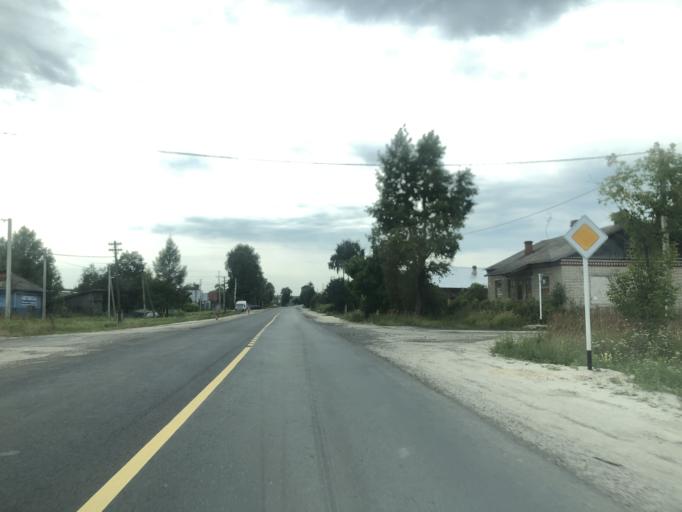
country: RU
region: Ivanovo
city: Pestyaki
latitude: 56.7054
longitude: 42.6852
